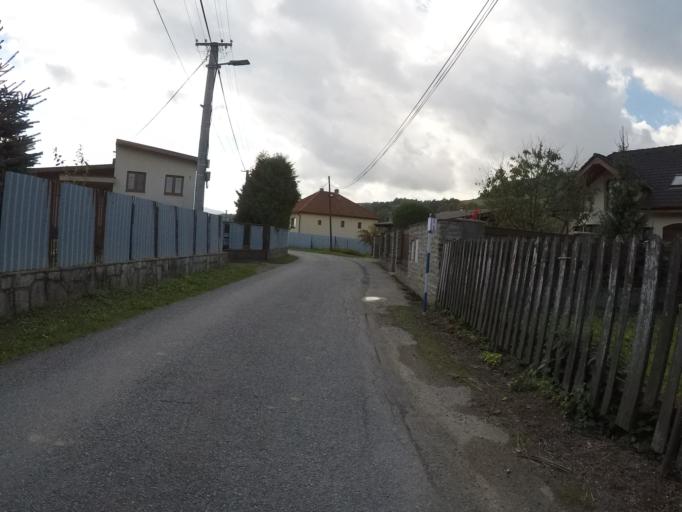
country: SK
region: Presovsky
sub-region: Okres Presov
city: Presov
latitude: 48.9377
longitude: 21.1795
